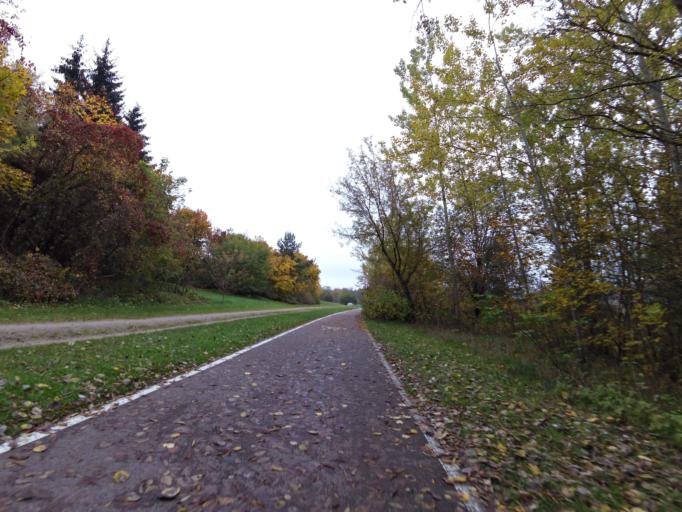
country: LT
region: Vilnius County
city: Rasos
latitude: 54.7203
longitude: 25.3095
